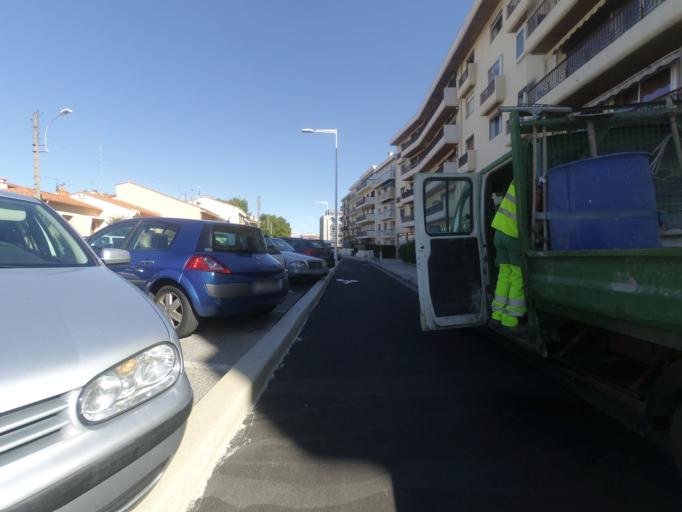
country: FR
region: Languedoc-Roussillon
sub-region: Departement des Pyrenees-Orientales
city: Perpignan
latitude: 42.6888
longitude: 2.9018
